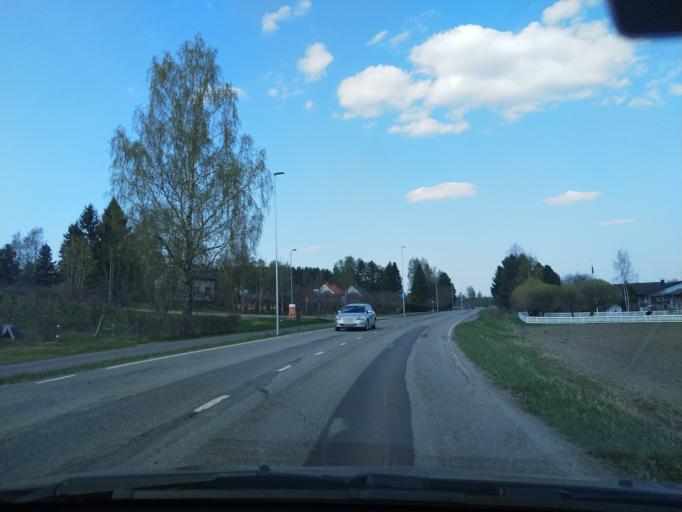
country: FI
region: Uusimaa
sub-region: Helsinki
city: Lohja
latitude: 60.1999
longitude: 24.0047
